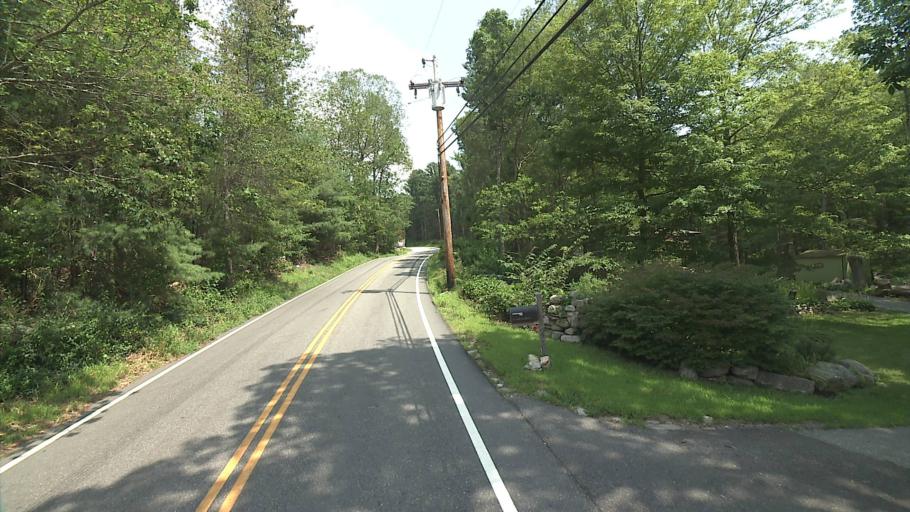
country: US
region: Connecticut
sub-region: Windham County
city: Danielson
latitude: 41.7737
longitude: -71.8427
